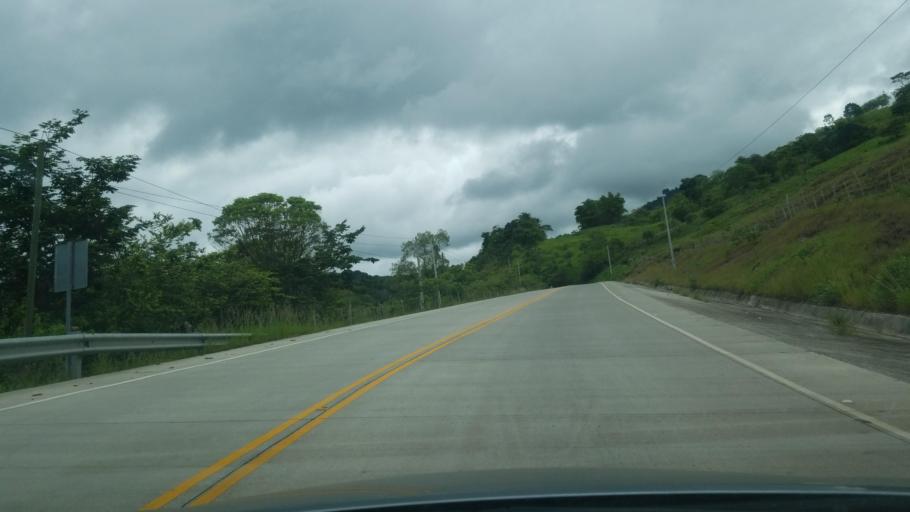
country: HN
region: Copan
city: San Jeronimo
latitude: 14.9574
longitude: -88.8978
